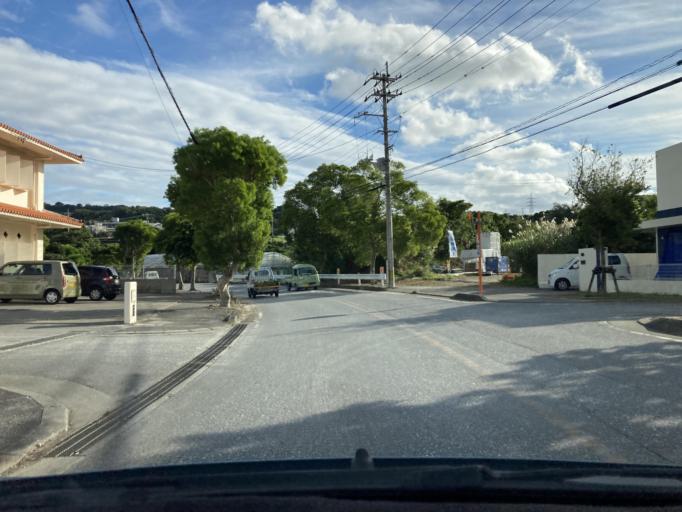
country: JP
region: Okinawa
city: Itoman
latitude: 26.1347
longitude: 127.6985
